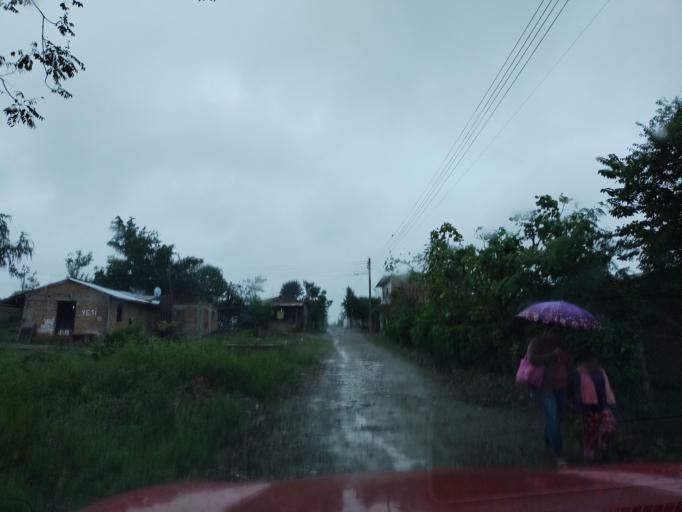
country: MX
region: Veracruz
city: Agua Dulce
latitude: 20.3341
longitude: -97.3223
